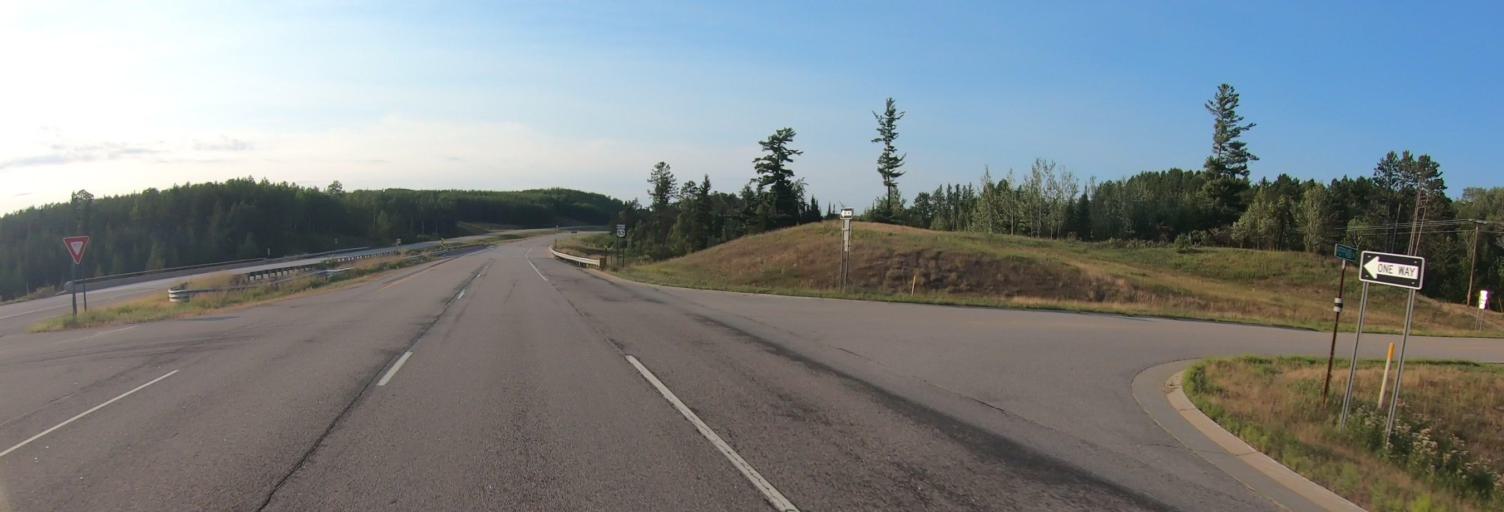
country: US
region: Minnesota
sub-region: Saint Louis County
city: Mountain Iron
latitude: 47.6773
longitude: -92.6353
